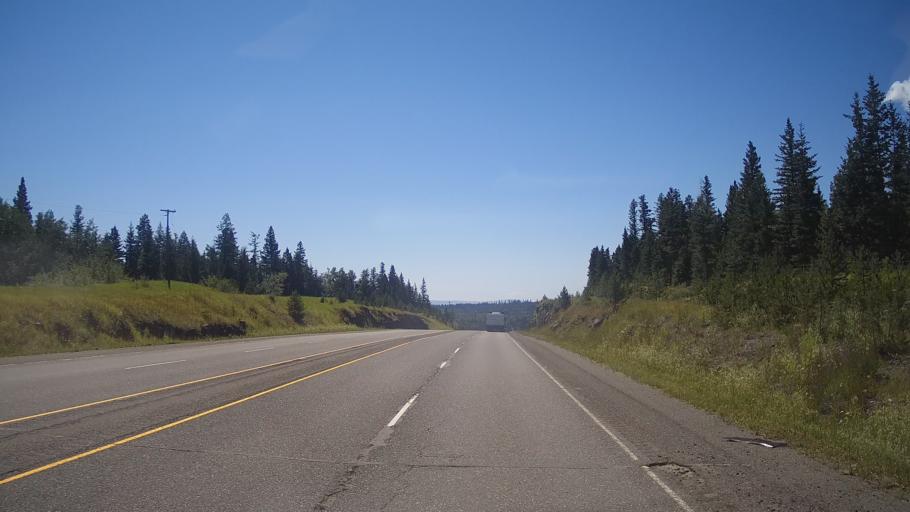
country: CA
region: British Columbia
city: Cache Creek
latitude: 51.4681
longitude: -121.3698
